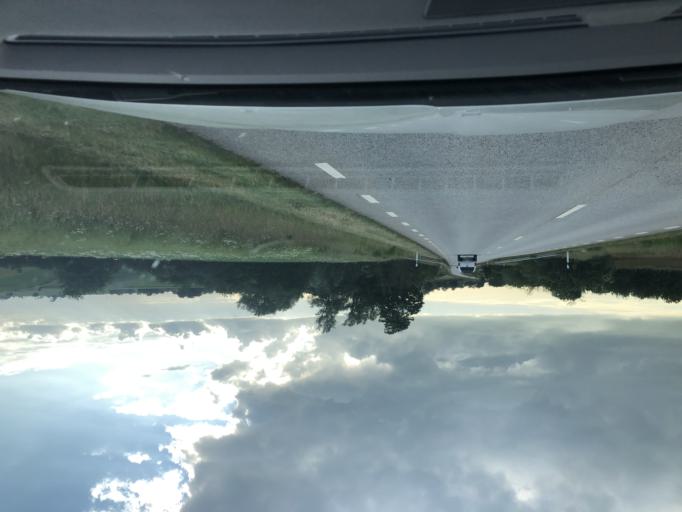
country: SE
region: Skane
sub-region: Simrishamns Kommun
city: Simrishamn
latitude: 55.5354
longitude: 14.3006
